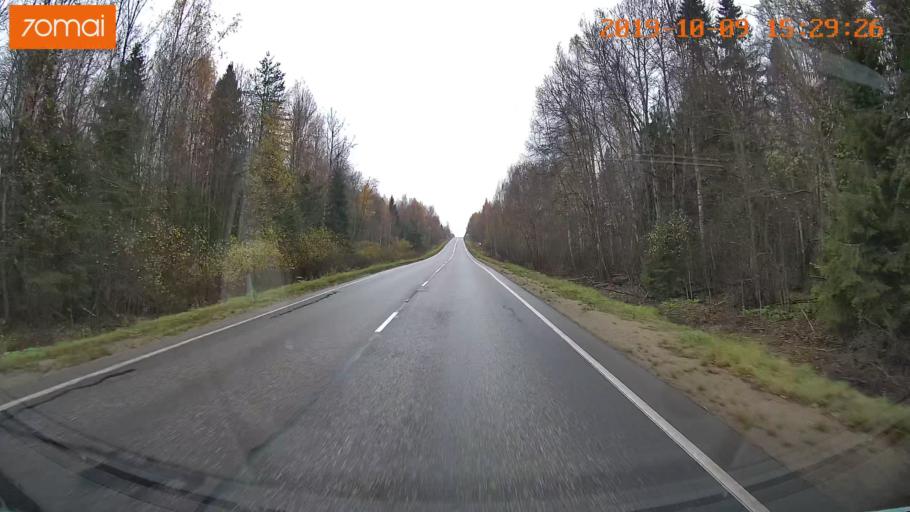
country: RU
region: Kostroma
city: Susanino
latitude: 57.9915
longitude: 41.3429
